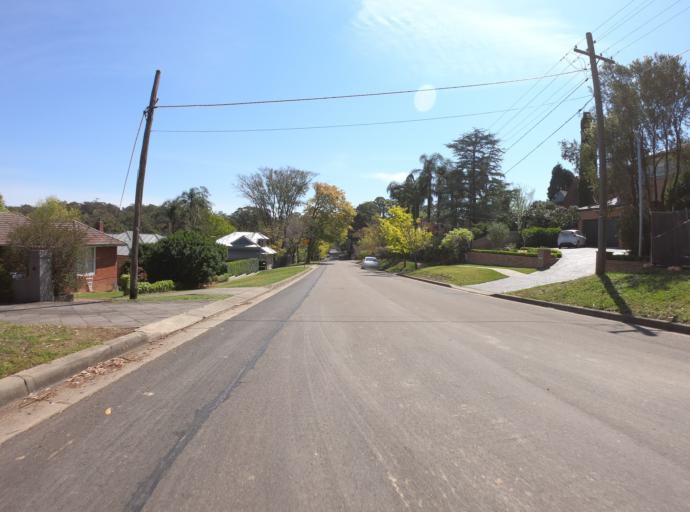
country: AU
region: New South Wales
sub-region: Hornsby Shire
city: Beecroft
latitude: -33.7514
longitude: 151.0586
